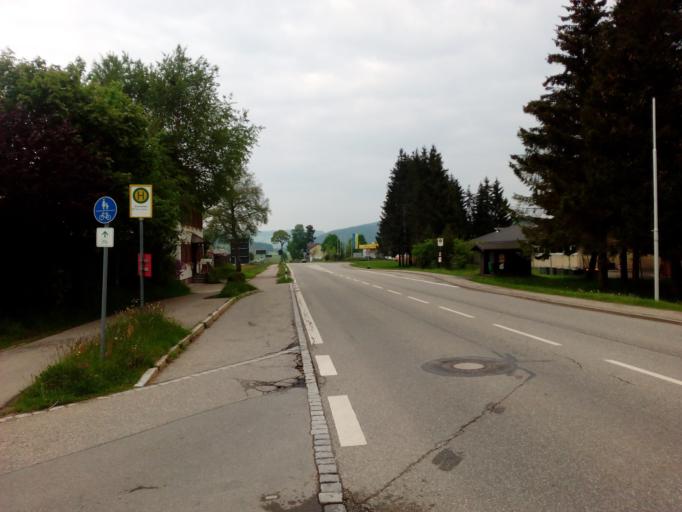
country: DE
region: Baden-Wuerttemberg
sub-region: Freiburg Region
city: Titisee-Neustadt
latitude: 47.9109
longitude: 8.1632
